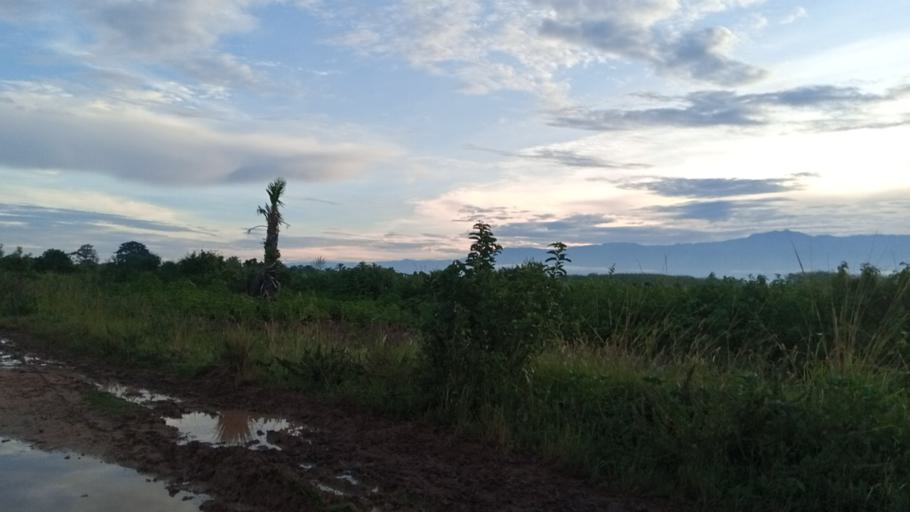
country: BI
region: Bujumbura Mairie
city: Bujumbura
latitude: -3.4678
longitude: 29.3420
